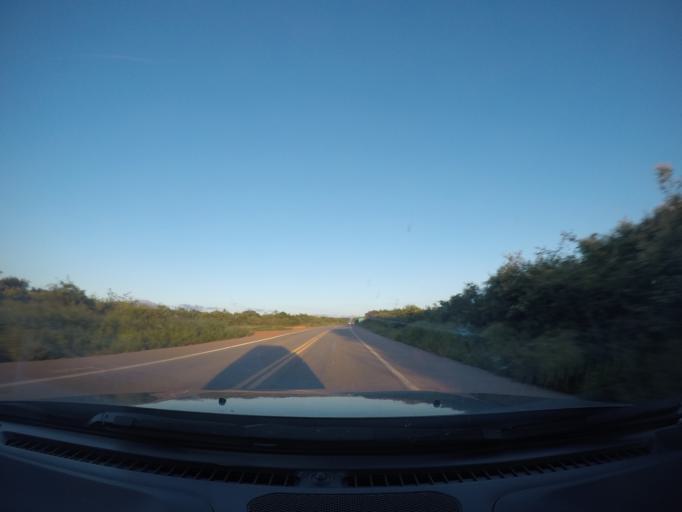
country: BR
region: Bahia
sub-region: Seabra
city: Seabra
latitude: -12.3934
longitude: -41.9252
